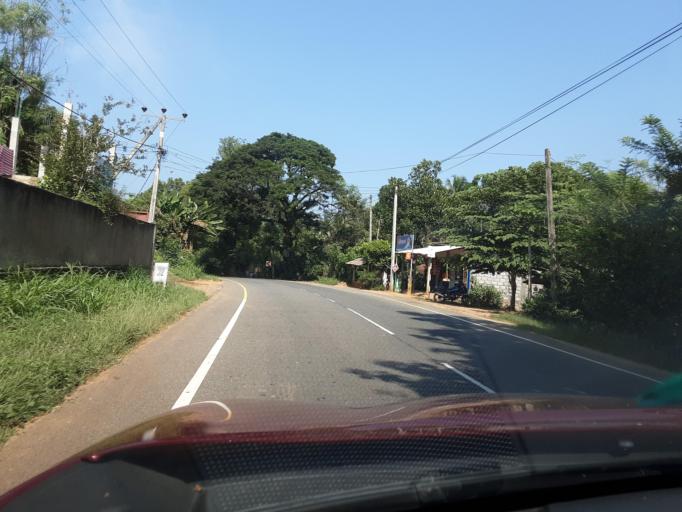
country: LK
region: Uva
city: Badulla
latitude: 7.1931
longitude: 81.0274
